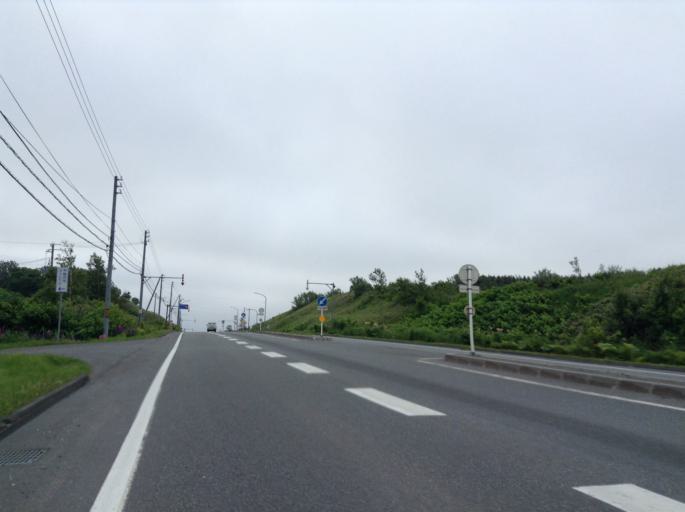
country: JP
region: Hokkaido
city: Wakkanai
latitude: 45.3746
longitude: 141.7146
